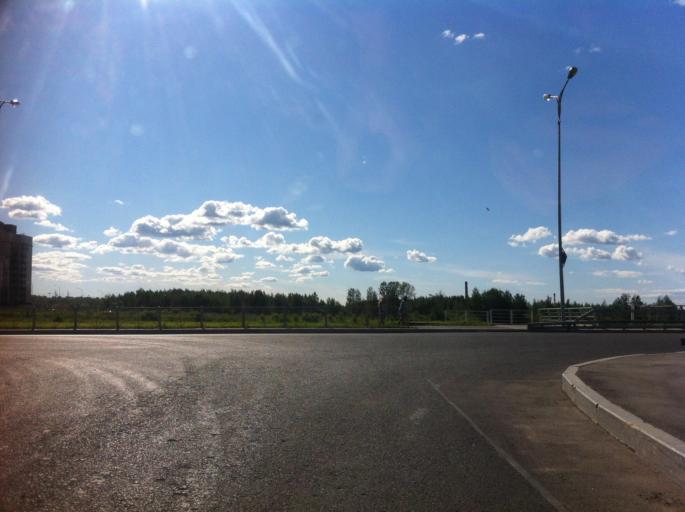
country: RU
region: St.-Petersburg
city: Sosnovaya Polyana
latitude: 59.8555
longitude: 30.1476
